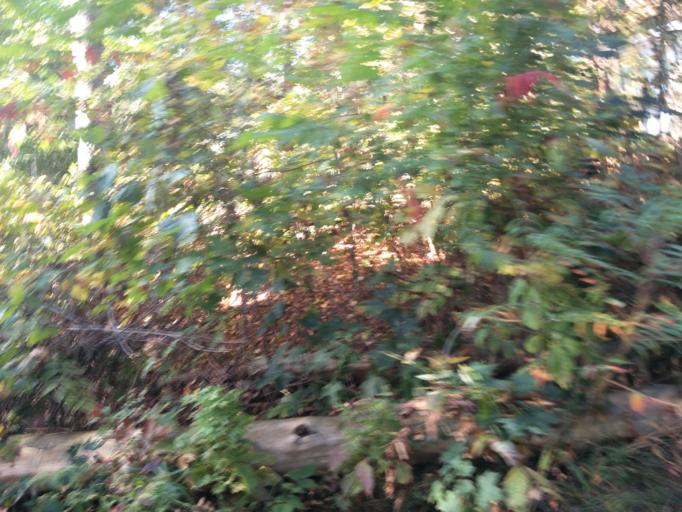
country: CA
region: Ontario
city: Perth
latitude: 44.6660
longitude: -76.5814
